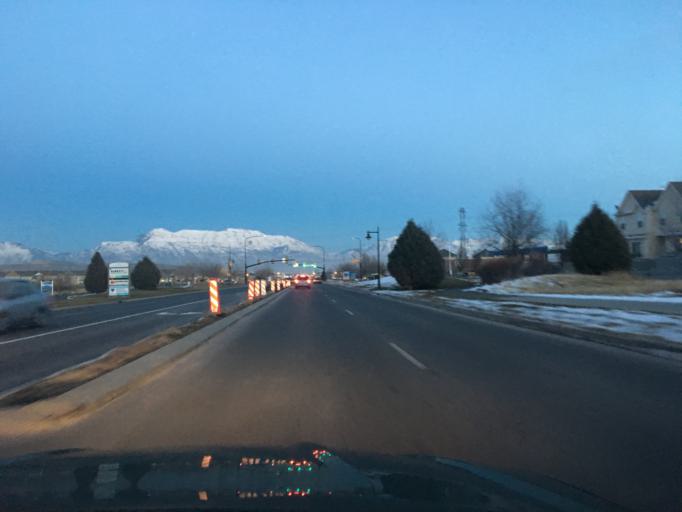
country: US
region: Utah
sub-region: Utah County
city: Eagle Mountain
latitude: 40.3622
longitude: -111.9786
